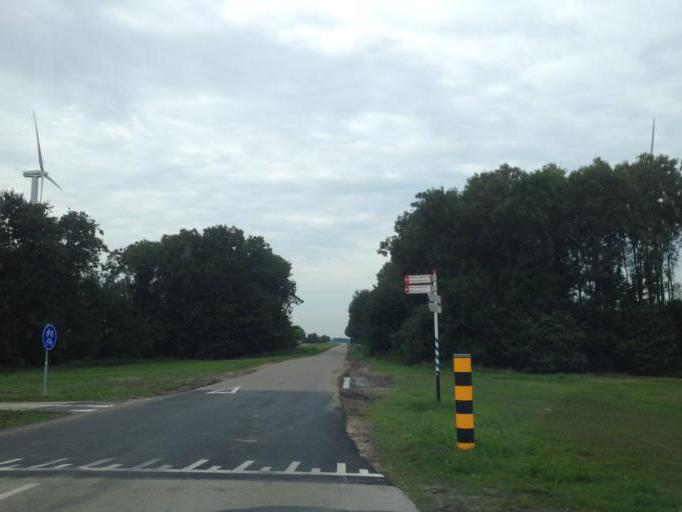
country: NL
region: Utrecht
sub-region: Gemeente Bunschoten
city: Spakenburg
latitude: 52.3592
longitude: 5.3583
